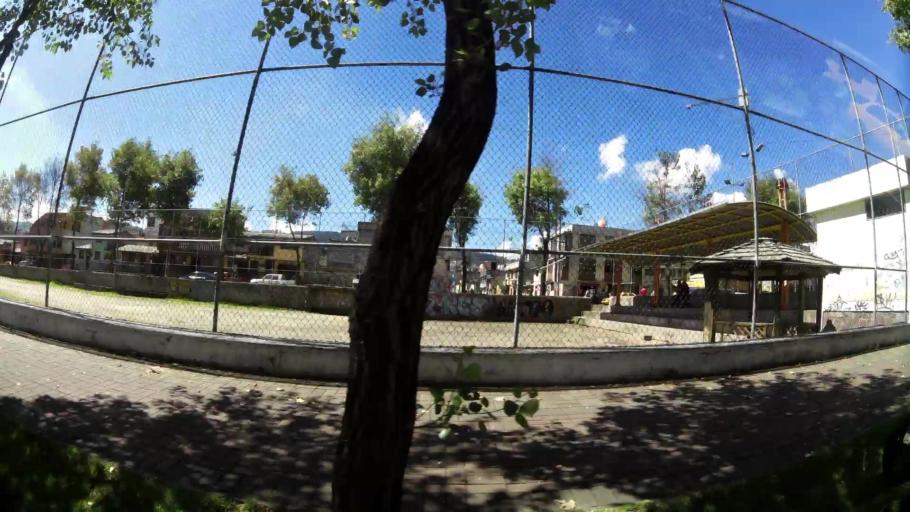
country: EC
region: Pichincha
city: Quito
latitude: -0.2602
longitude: -78.5354
